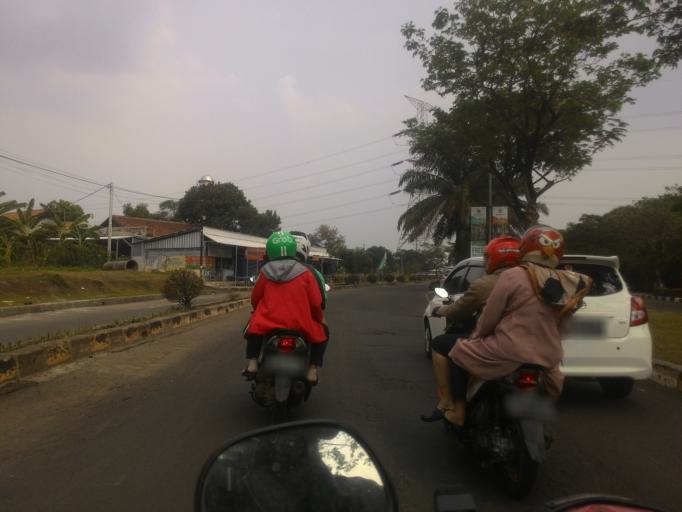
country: ID
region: West Java
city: Depok
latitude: -6.4161
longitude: 106.8210
